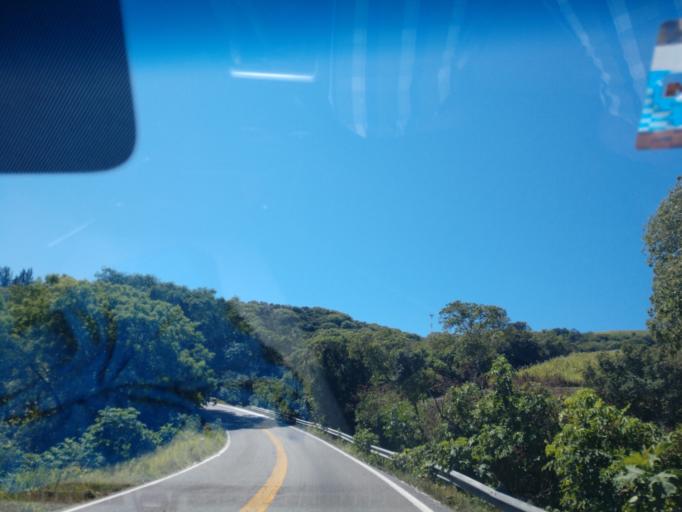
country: MX
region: Nayarit
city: Xalisco
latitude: 21.3633
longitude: -104.9197
